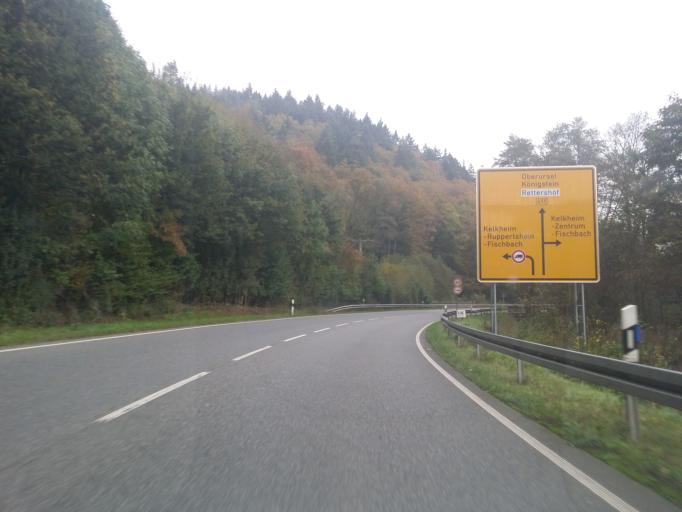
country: DE
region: Hesse
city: Eppstein
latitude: 50.1507
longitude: 8.4101
